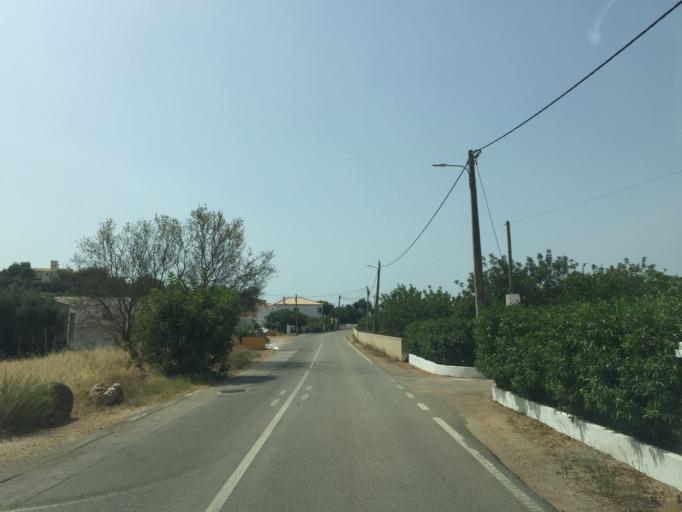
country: PT
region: Faro
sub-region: Loule
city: Boliqueime
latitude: 37.1326
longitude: -8.1411
